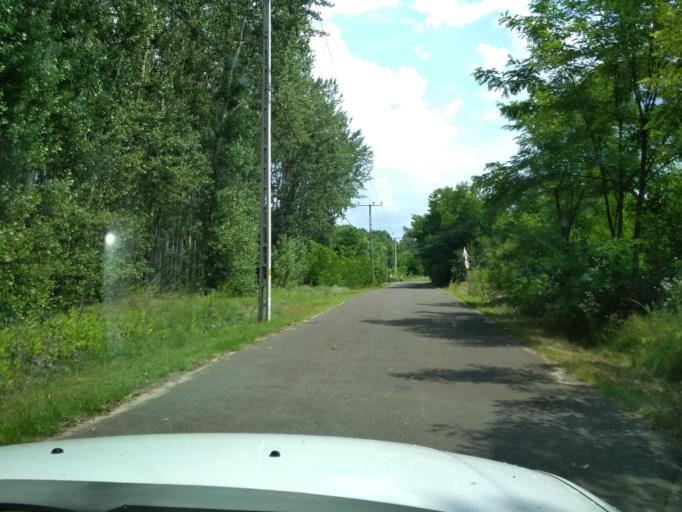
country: HU
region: Pest
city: Nagykata
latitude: 47.3822
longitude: 19.7570
